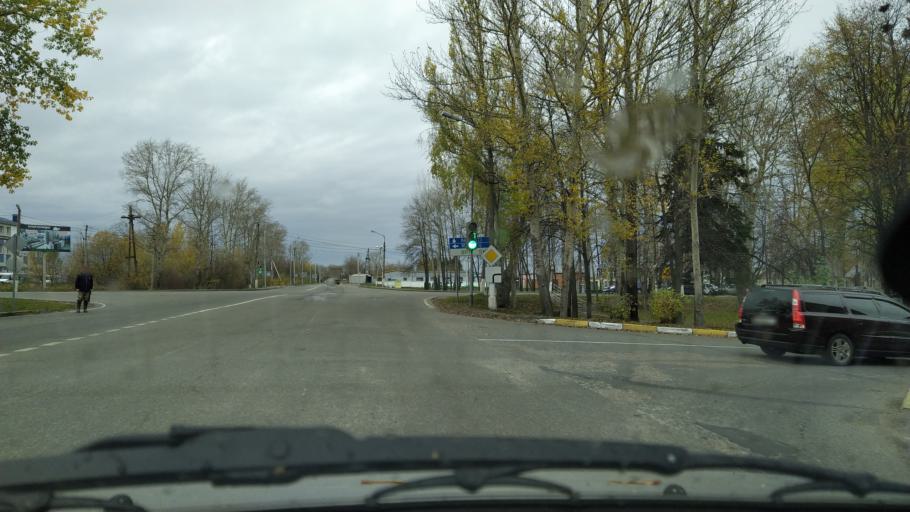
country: RU
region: Moskovskaya
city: Voskresensk
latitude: 55.3167
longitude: 38.6487
